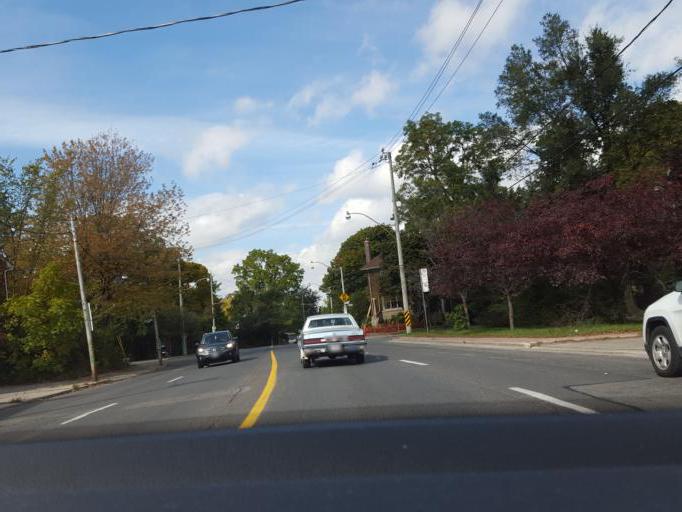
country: CA
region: Ontario
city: Toronto
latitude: 43.7165
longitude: -79.3932
